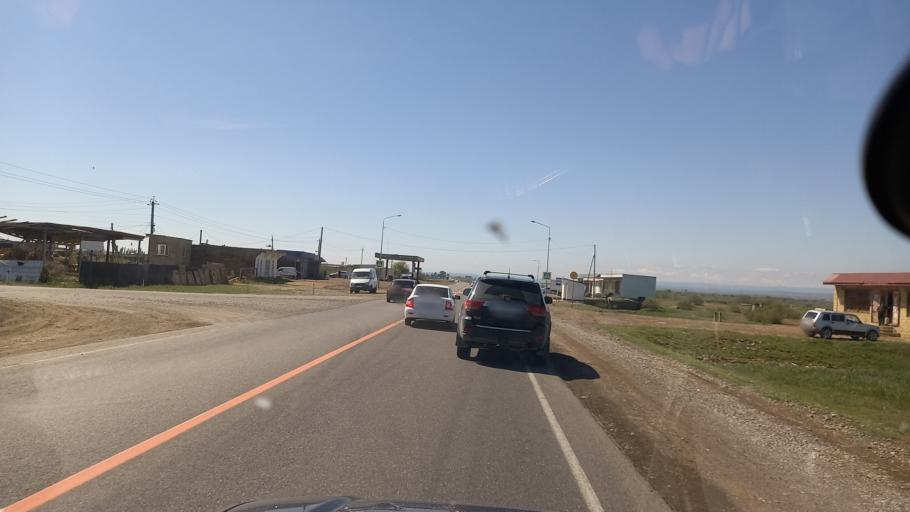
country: RU
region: Dagestan
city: Khazar
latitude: 41.9403
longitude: 48.3263
